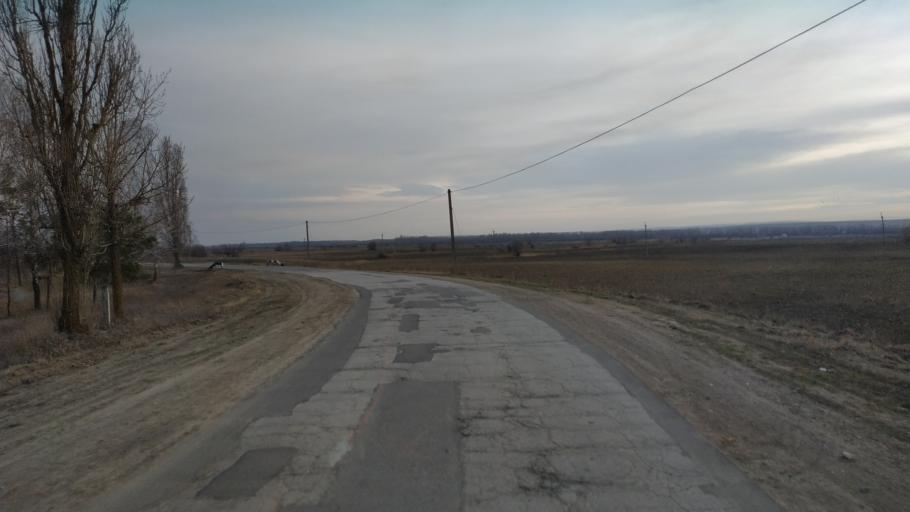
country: MD
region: Hincesti
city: Dancu
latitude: 46.7972
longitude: 28.1824
